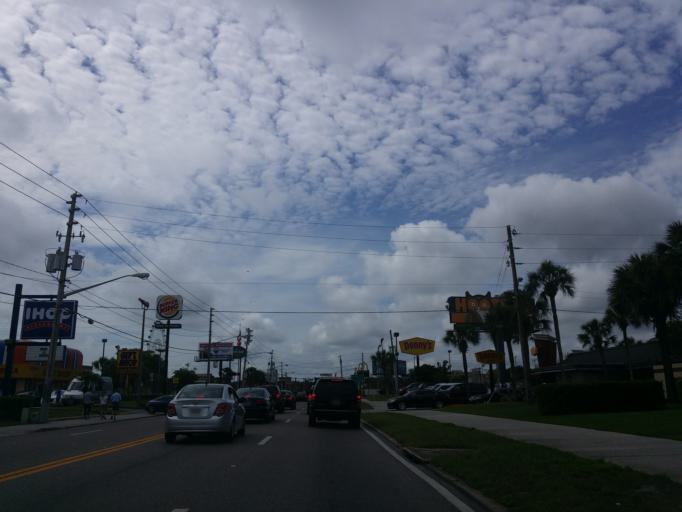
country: US
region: Florida
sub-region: Orange County
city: Doctor Phillips
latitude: 28.4522
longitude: -81.4709
